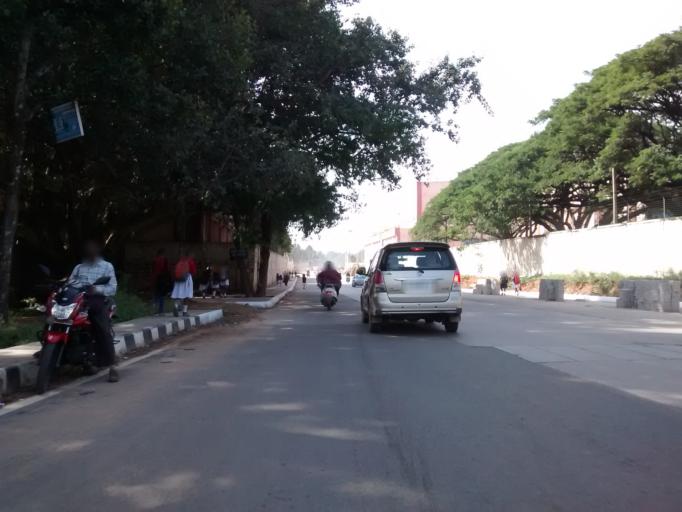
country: IN
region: Karnataka
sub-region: Bangalore Urban
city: Bangalore
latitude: 12.9688
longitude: 77.6602
